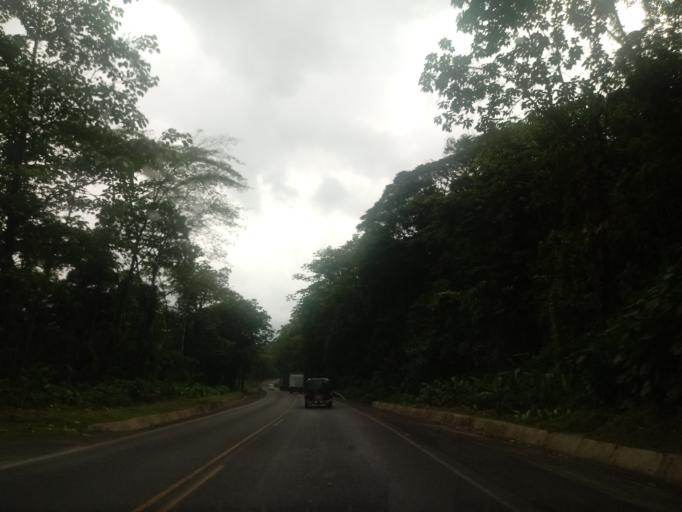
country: CR
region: San Jose
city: Dulce Nombre de Jesus
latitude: 10.1493
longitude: -83.9435
